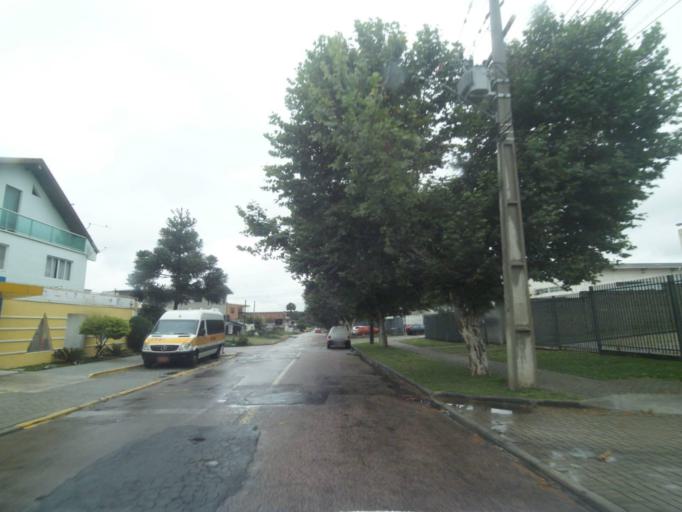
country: BR
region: Parana
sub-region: Araucaria
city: Araucaria
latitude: -25.5388
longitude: -49.3387
